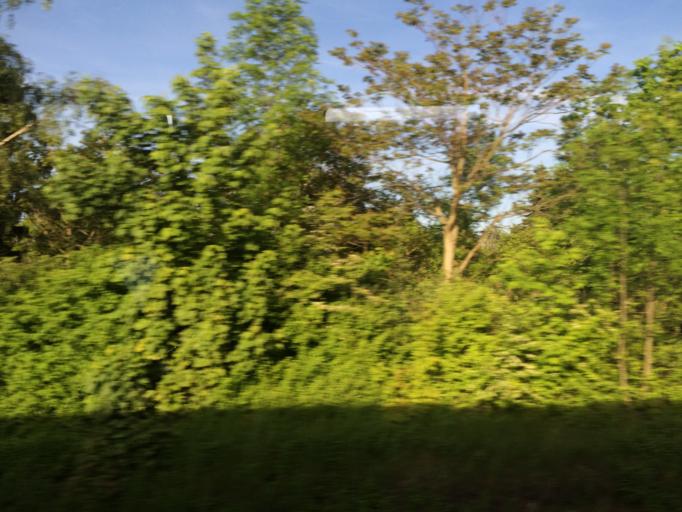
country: DE
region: Rheinland-Pfalz
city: Mainz
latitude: 50.0175
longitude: 8.2778
